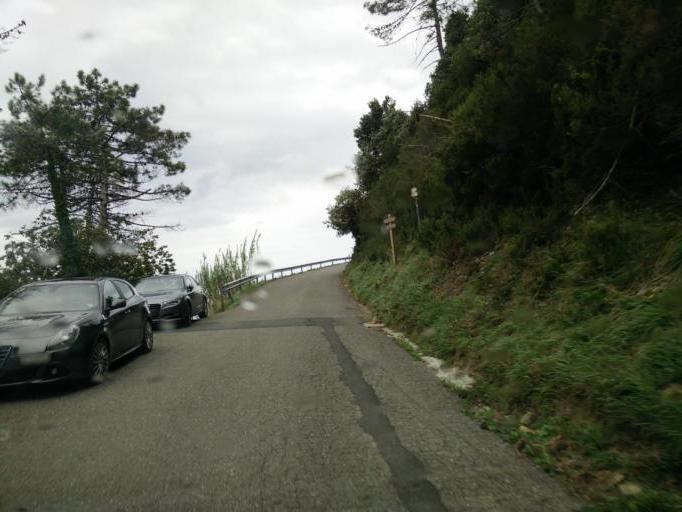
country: IT
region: Liguria
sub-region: Provincia di La Spezia
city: Vernazza
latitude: 44.1435
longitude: 9.6867
